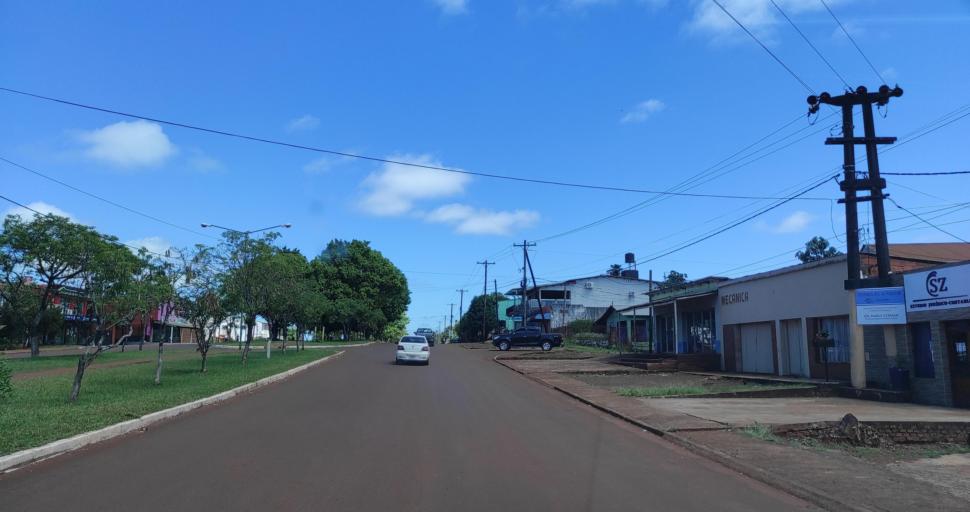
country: AR
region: Misiones
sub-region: Departamento de Veinticinco de Mayo
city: Veinticinco de Mayo
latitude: -27.3739
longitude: -54.7463
